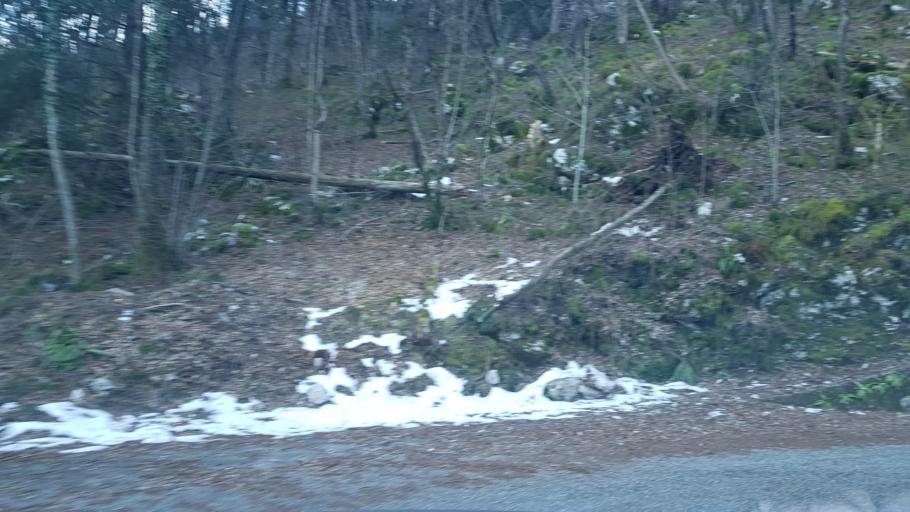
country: IT
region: Friuli Venezia Giulia
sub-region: Provincia di Udine
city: Trasaghis
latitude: 46.2902
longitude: 13.0340
